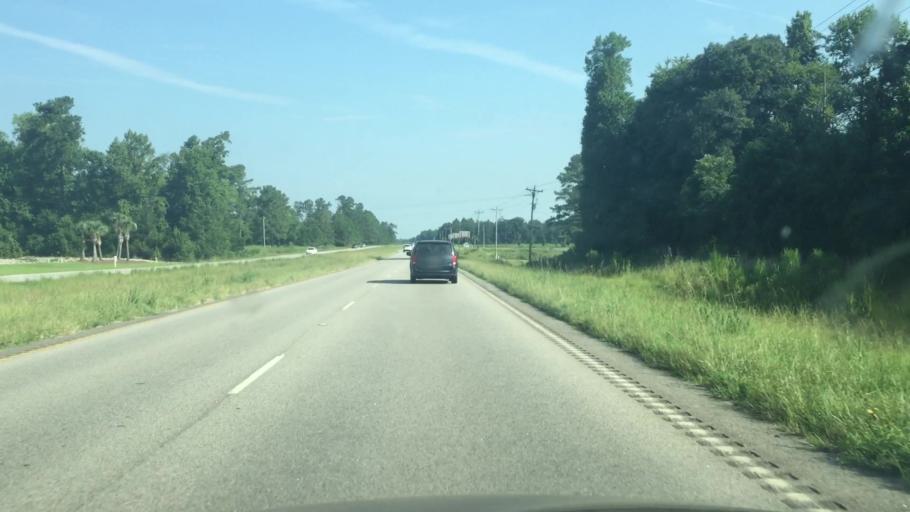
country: US
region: South Carolina
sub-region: Horry County
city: Little River
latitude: 33.9662
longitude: -78.7393
